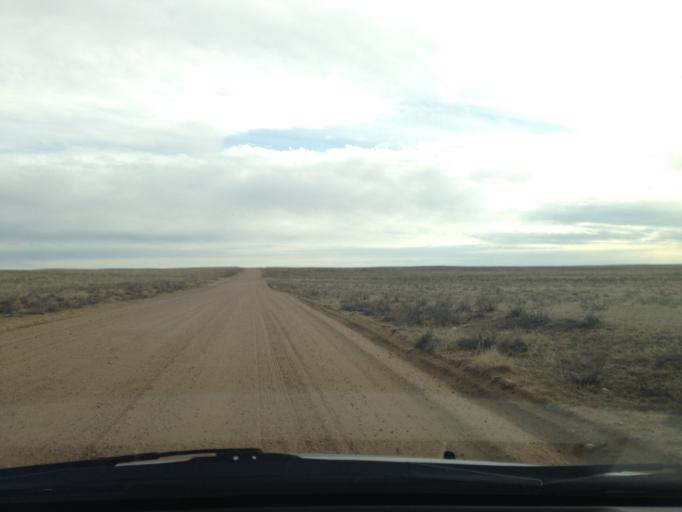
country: US
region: Colorado
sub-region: Weld County
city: Keenesburg
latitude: 40.2416
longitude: -104.2068
